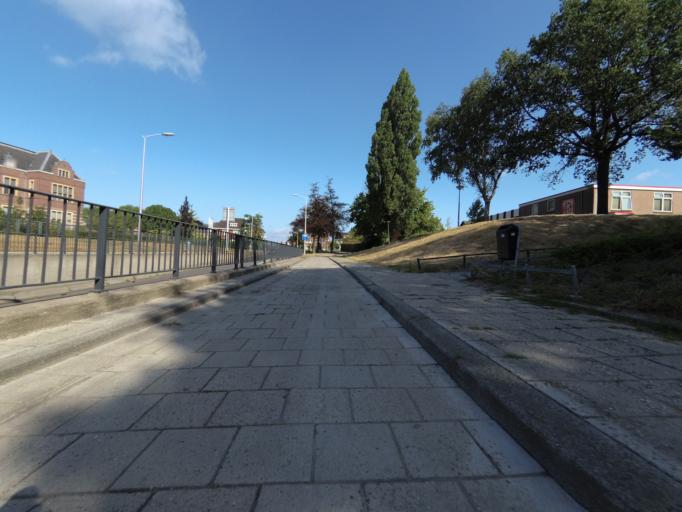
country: NL
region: Overijssel
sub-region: Gemeente Oldenzaal
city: Oldenzaal
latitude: 52.3061
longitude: 6.9306
